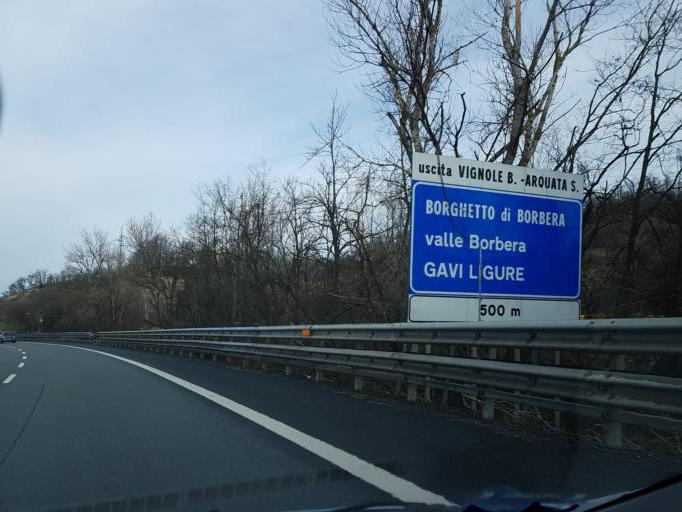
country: IT
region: Piedmont
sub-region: Provincia di Alessandria
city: Vignole Borbera
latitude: 44.6982
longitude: 8.8943
